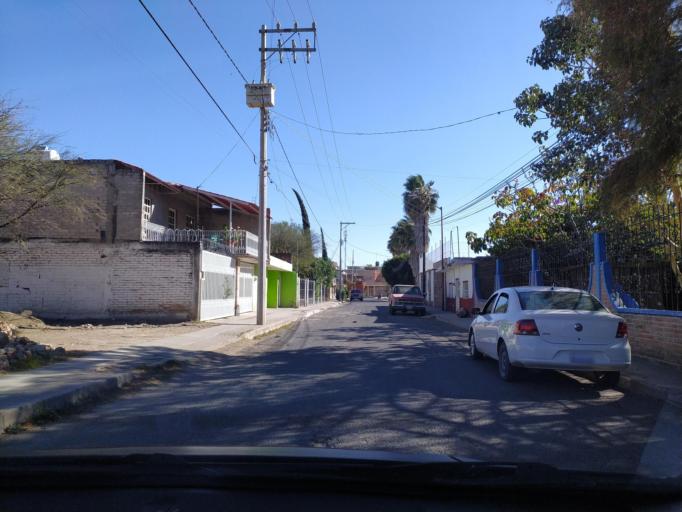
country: MX
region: Guanajuato
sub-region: San Francisco del Rincon
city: Estacion de San Francisco
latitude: 21.0247
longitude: -101.8323
